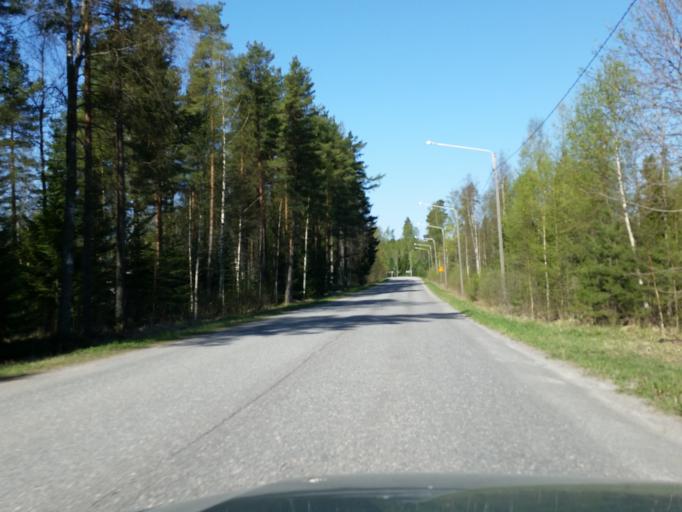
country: FI
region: Uusimaa
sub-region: Helsinki
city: Karjalohja
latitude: 60.1402
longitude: 23.8557
